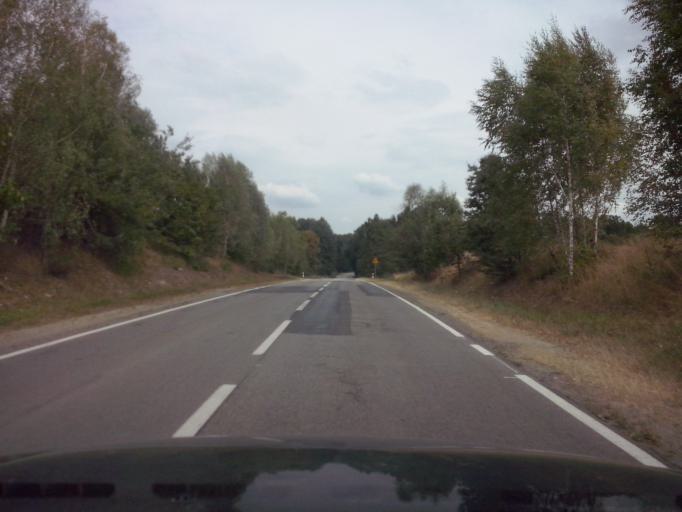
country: PL
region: Swietokrzyskie
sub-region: Powiat kielecki
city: Rakow
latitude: 50.7150
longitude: 21.0601
